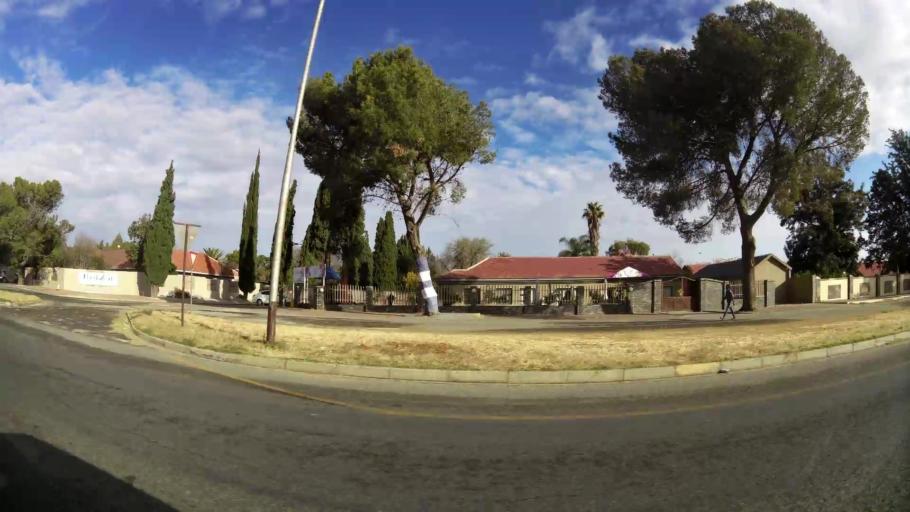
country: ZA
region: Orange Free State
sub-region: Lejweleputswa District Municipality
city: Welkom
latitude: -27.9763
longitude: 26.7238
